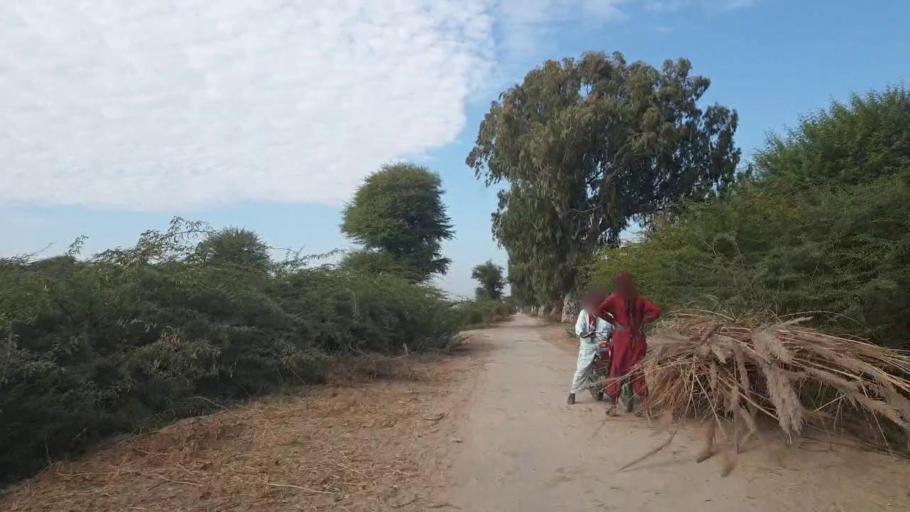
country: PK
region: Sindh
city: Sinjhoro
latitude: 26.0418
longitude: 68.8772
